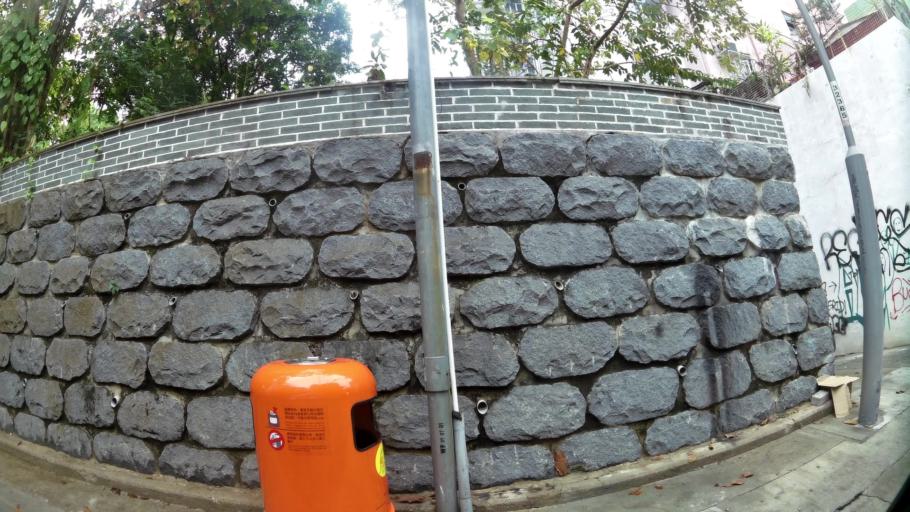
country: HK
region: Central and Western
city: Central
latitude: 22.2499
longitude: 114.1557
